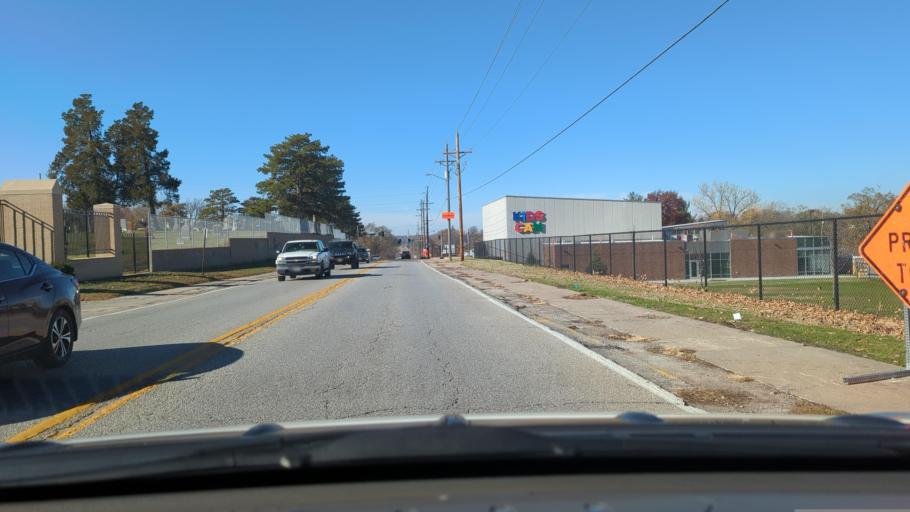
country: US
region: Nebraska
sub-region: Sarpy County
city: La Vista
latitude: 41.2054
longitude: -95.9842
